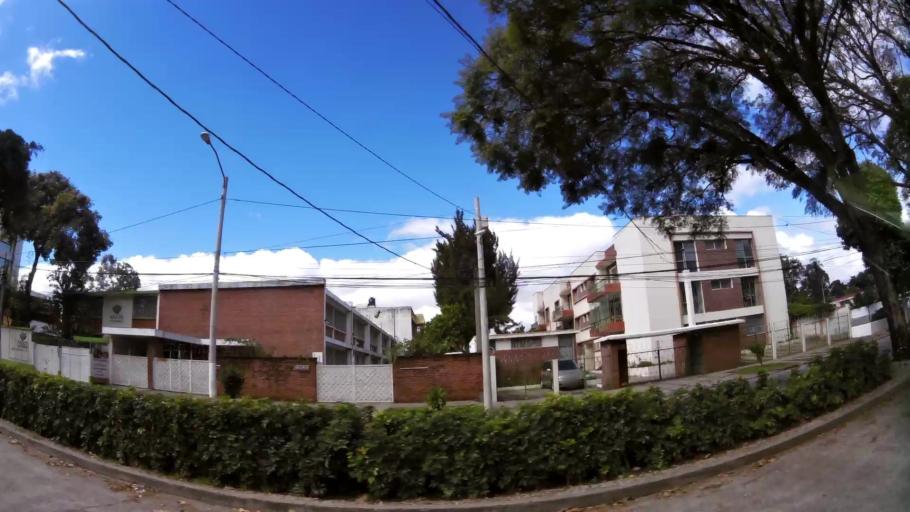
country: GT
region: Guatemala
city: Guatemala City
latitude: 14.6056
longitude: -90.5242
